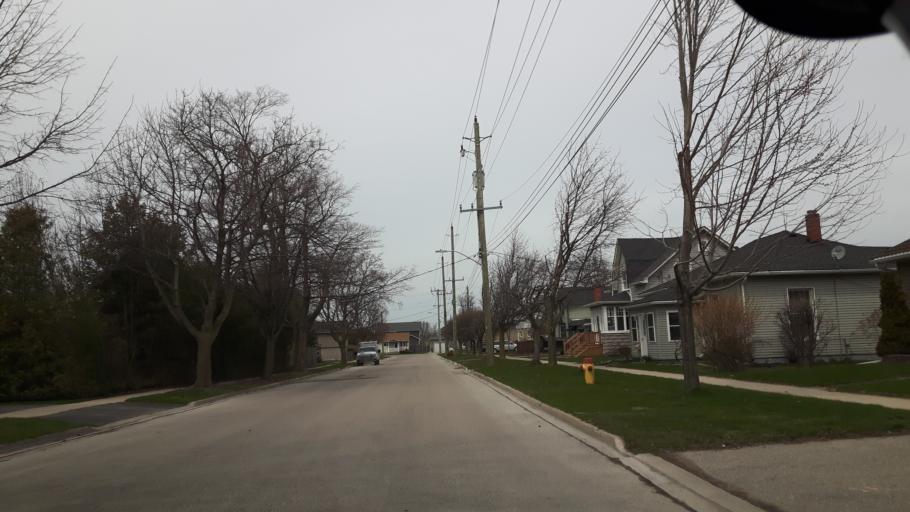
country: CA
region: Ontario
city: Goderich
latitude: 43.7389
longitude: -81.7004
